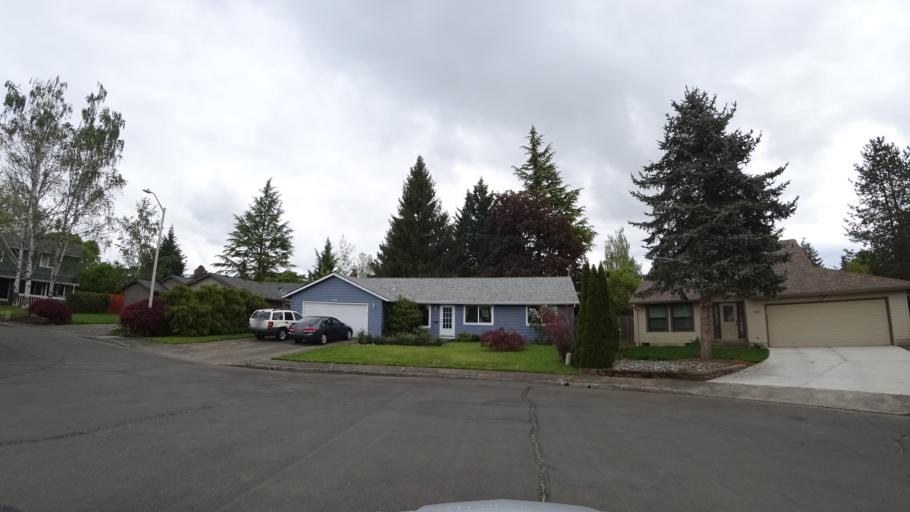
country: US
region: Oregon
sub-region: Washington County
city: Hillsboro
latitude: 45.5392
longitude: -122.9828
